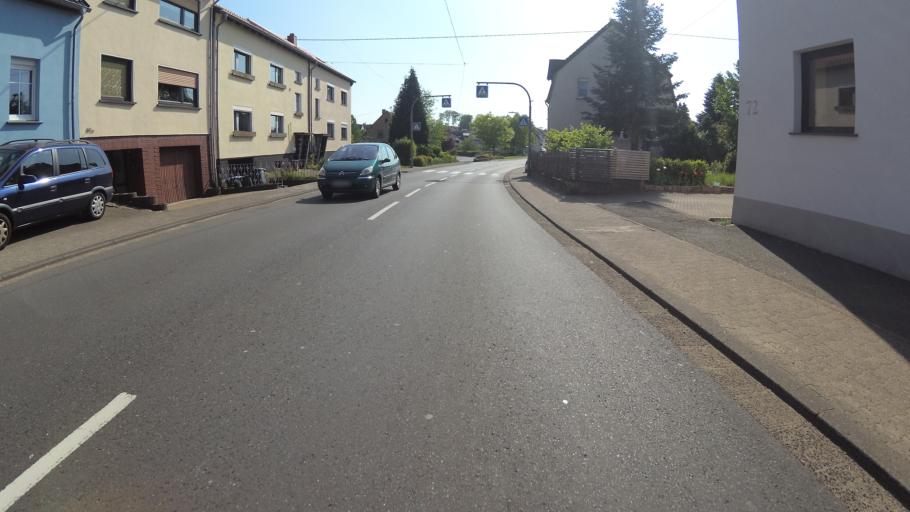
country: DE
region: Saarland
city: Illingen
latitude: 49.3659
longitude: 7.0797
